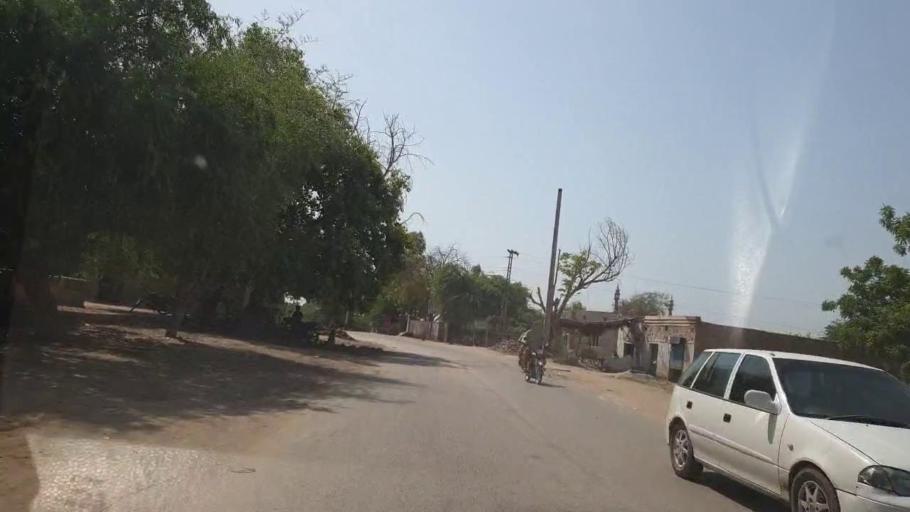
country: PK
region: Sindh
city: Bozdar
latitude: 27.1228
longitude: 68.5447
